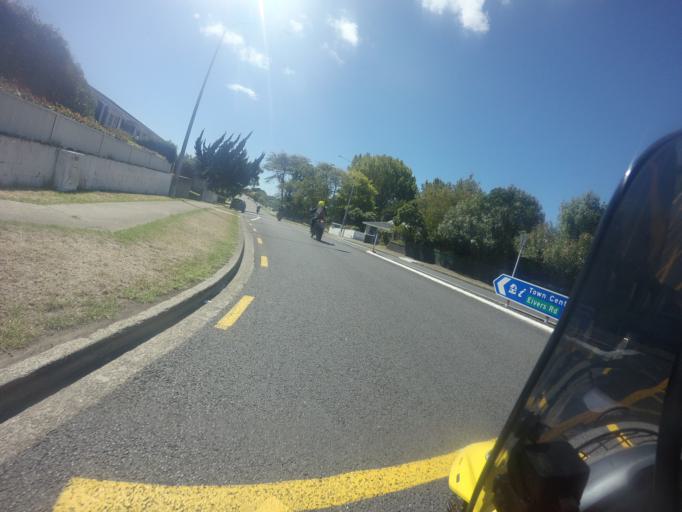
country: NZ
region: Bay of Plenty
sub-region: Whakatane District
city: Whakatane
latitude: -37.9583
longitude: 176.9814
